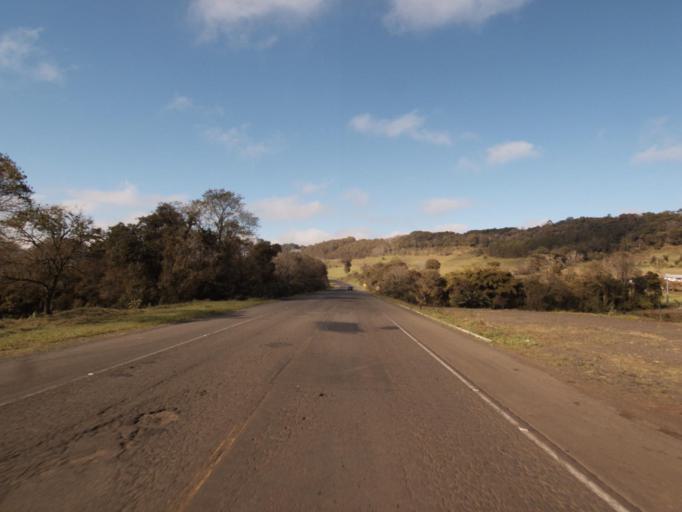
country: BR
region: Rio Grande do Sul
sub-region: Frederico Westphalen
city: Frederico Westphalen
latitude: -27.0526
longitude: -53.2290
